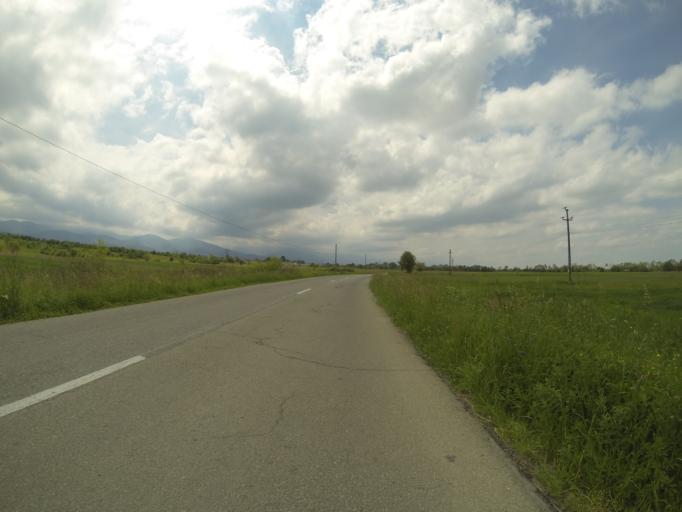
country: RO
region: Brasov
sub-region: Comuna Sinca Veche
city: Sinca Veche
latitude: 45.7529
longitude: 25.1330
